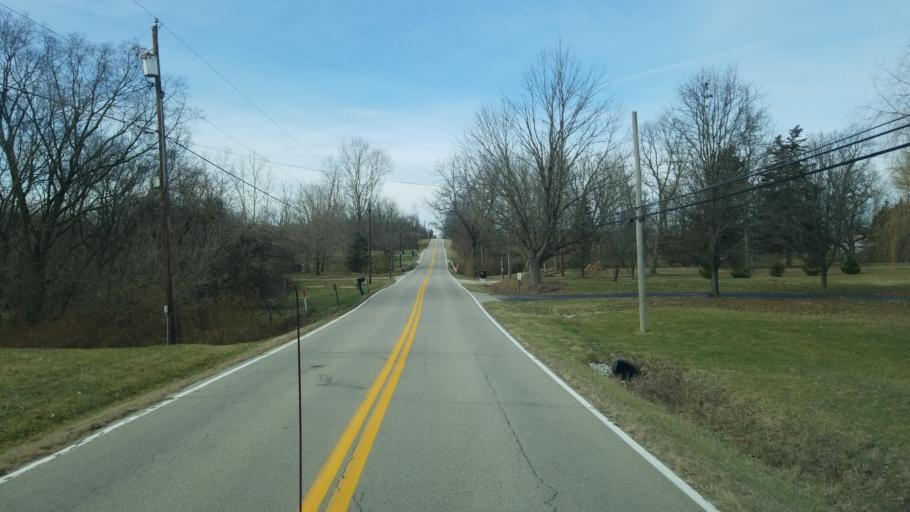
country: US
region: Ohio
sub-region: Warren County
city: Lebanon
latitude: 39.4290
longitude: -84.1423
